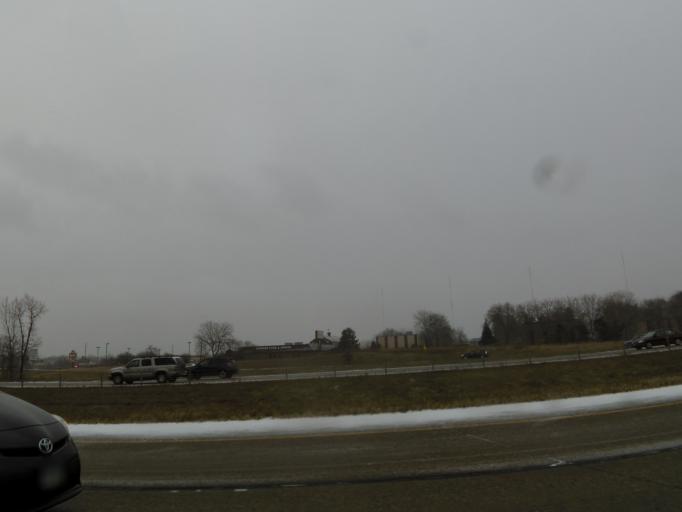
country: US
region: Minnesota
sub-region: Dakota County
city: Eagan
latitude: 44.7885
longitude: -93.2211
